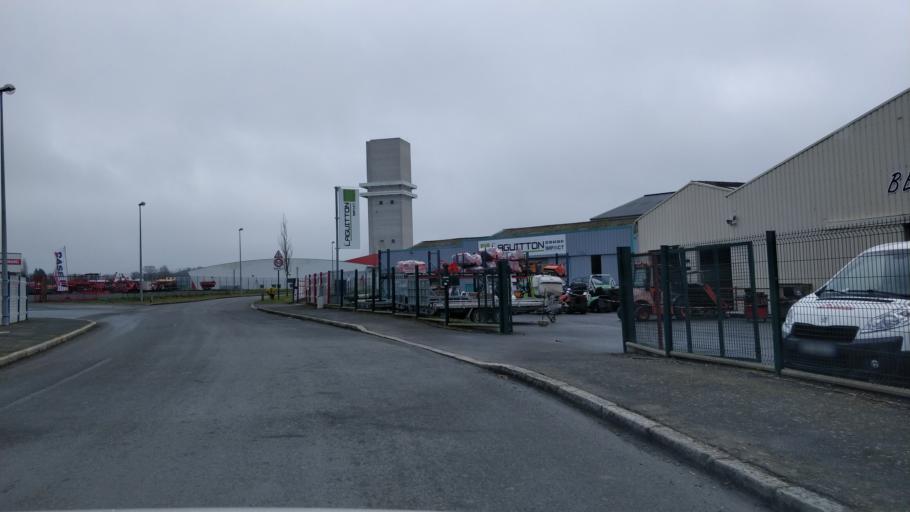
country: FR
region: Brittany
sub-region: Departement des Cotes-d'Armor
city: Broons
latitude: 48.3161
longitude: -2.2496
